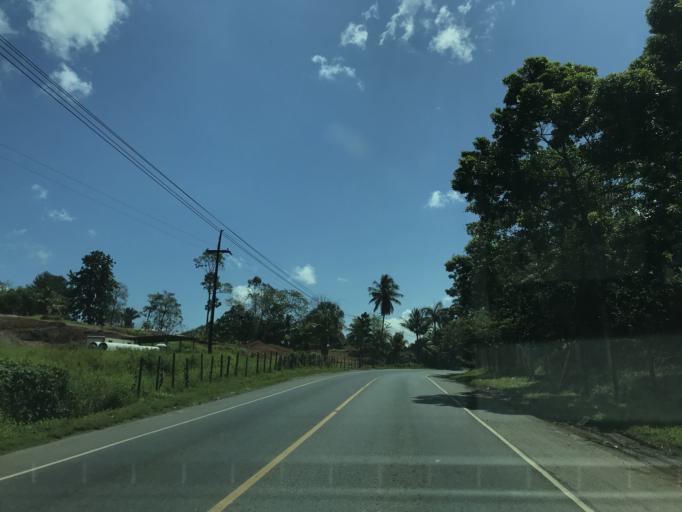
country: GT
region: Izabal
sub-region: Municipio de Puerto Barrios
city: Puerto Barrios
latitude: 15.6628
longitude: -88.5515
